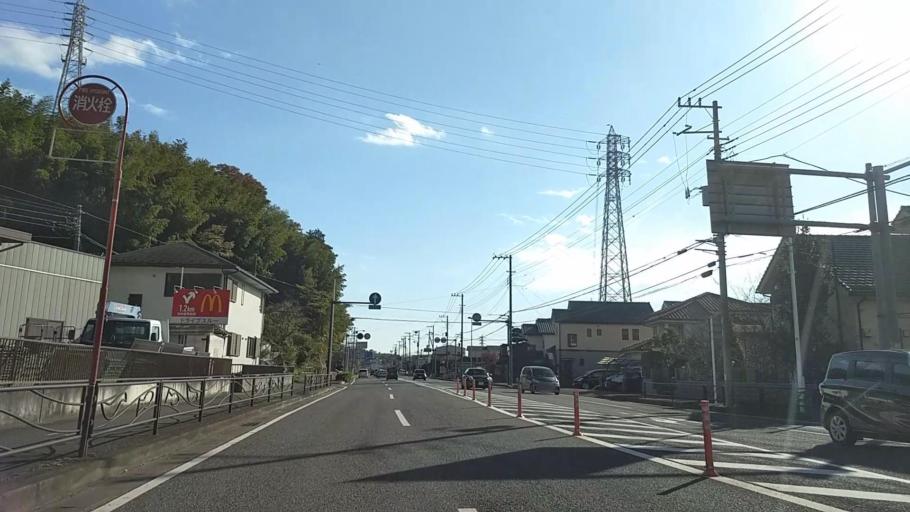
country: JP
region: Tokyo
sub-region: Machida-shi
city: Machida
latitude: 35.5690
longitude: 139.5136
